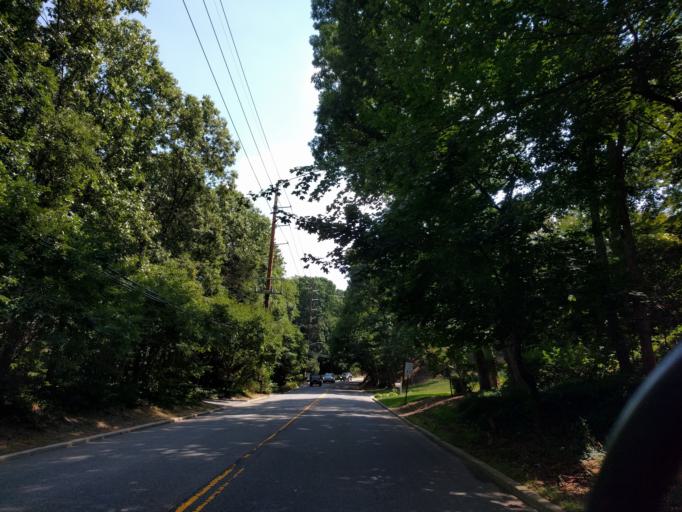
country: US
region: New York
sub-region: Nassau County
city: East Norwich
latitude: 40.8454
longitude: -73.5254
